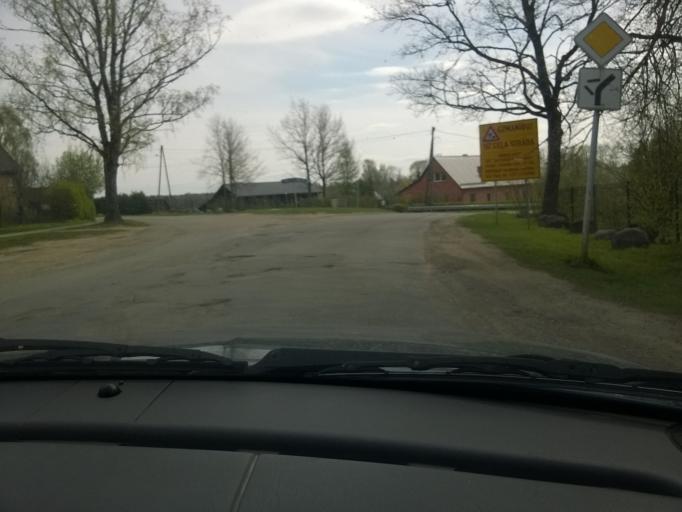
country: LV
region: Vilanu
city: Vilani
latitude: 56.5420
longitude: 26.9269
